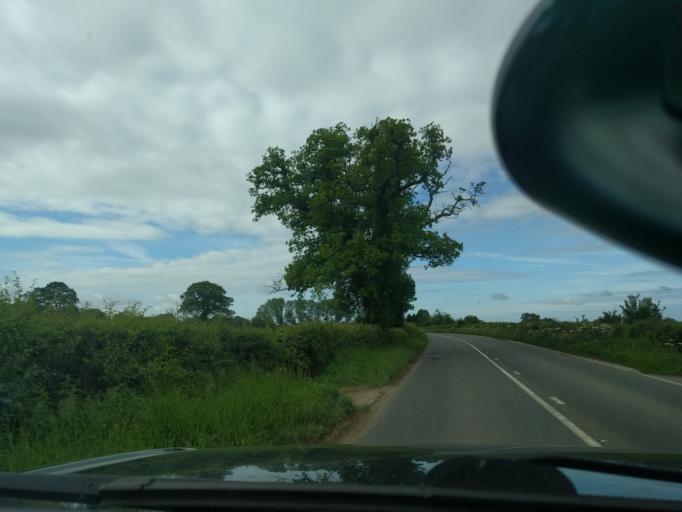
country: GB
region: England
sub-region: Wiltshire
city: Calne
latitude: 51.4591
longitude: -1.9902
